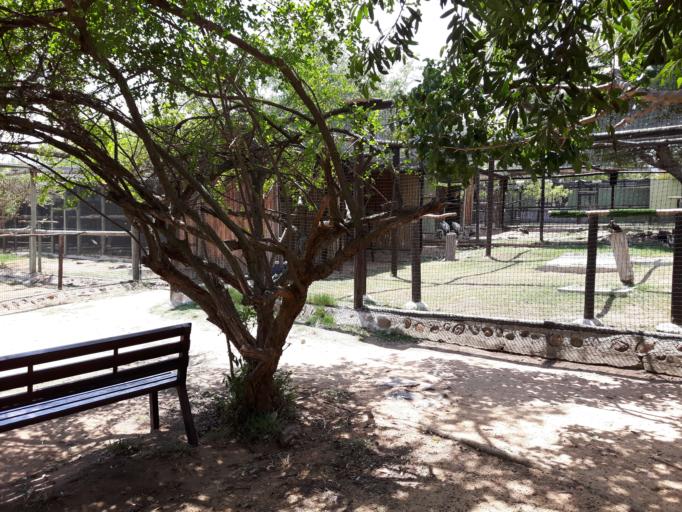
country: ZA
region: Limpopo
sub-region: Mopani District Municipality
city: Hoedspruit
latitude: -24.5151
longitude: 30.9042
